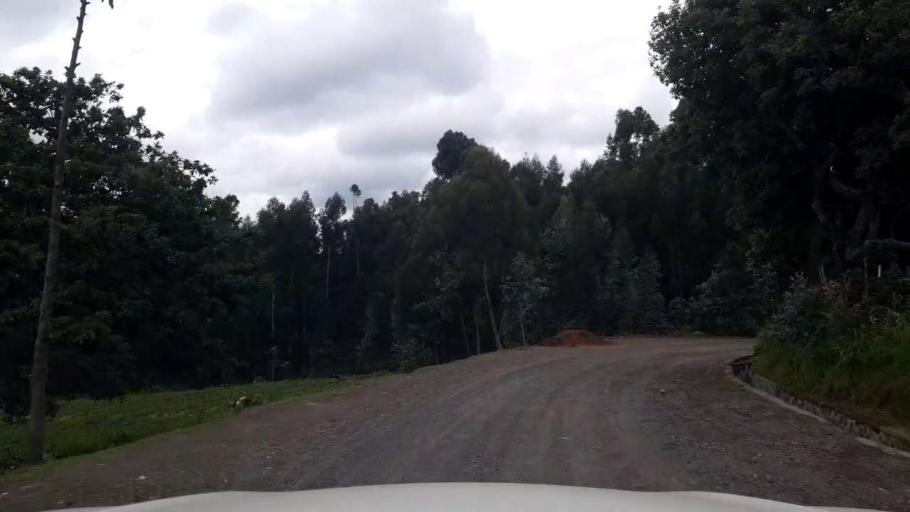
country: RW
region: Northern Province
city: Musanze
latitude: -1.5398
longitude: 29.5344
